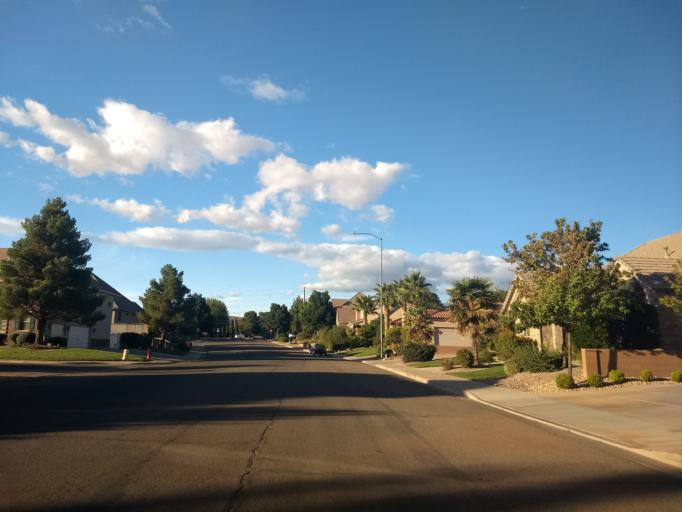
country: US
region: Utah
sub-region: Washington County
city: Saint George
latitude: 37.0909
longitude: -113.5641
